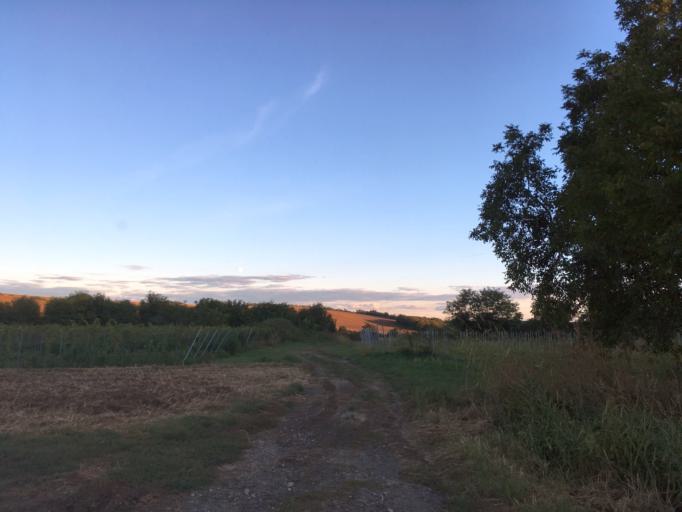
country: SK
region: Nitriansky
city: Svodin
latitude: 47.9117
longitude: 18.4408
